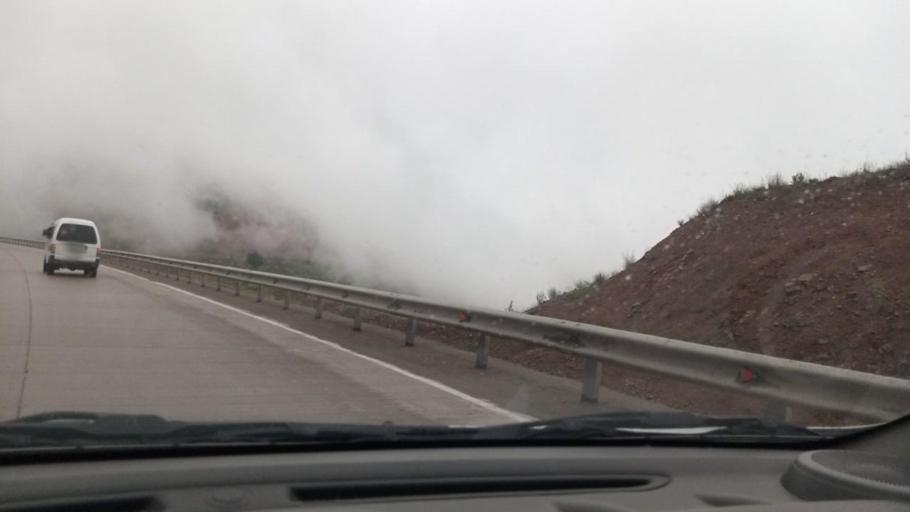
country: UZ
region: Toshkent
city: Angren
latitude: 41.1107
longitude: 70.5034
